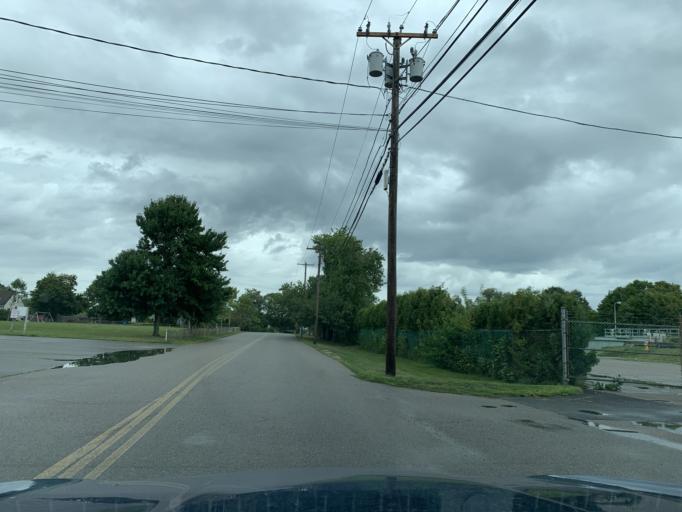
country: US
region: Rhode Island
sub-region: Bristol County
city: Warren
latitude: 41.7295
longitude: -71.2656
